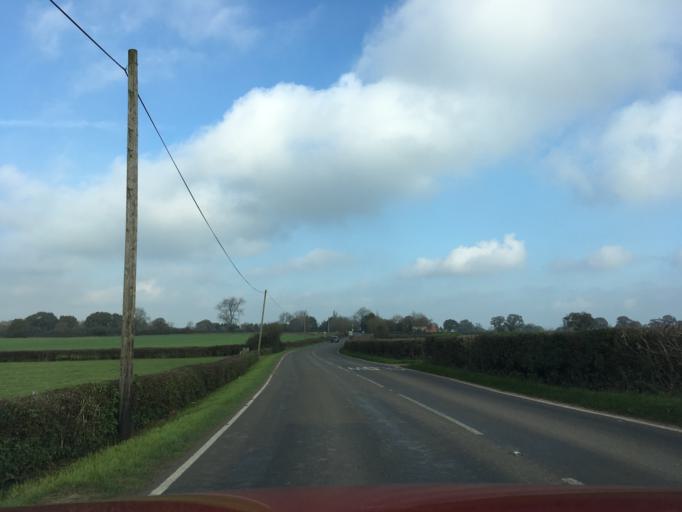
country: GB
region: England
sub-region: South Gloucestershire
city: Tytherington
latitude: 51.5946
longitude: -2.4449
